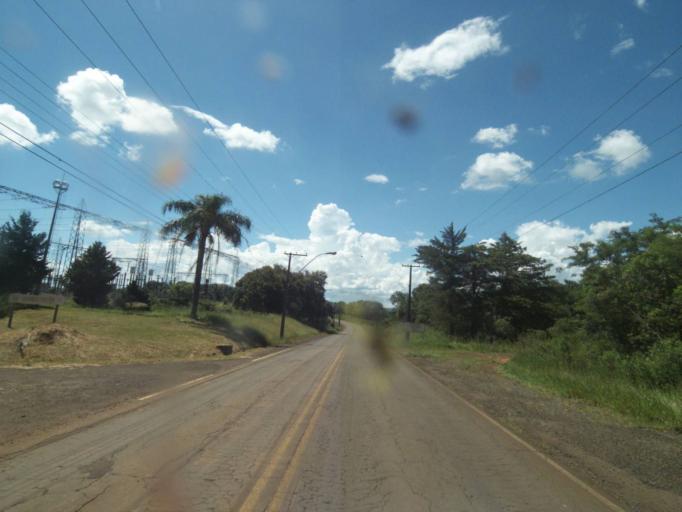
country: BR
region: Parana
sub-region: Chopinzinho
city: Chopinzinho
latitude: -25.7891
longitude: -52.0946
